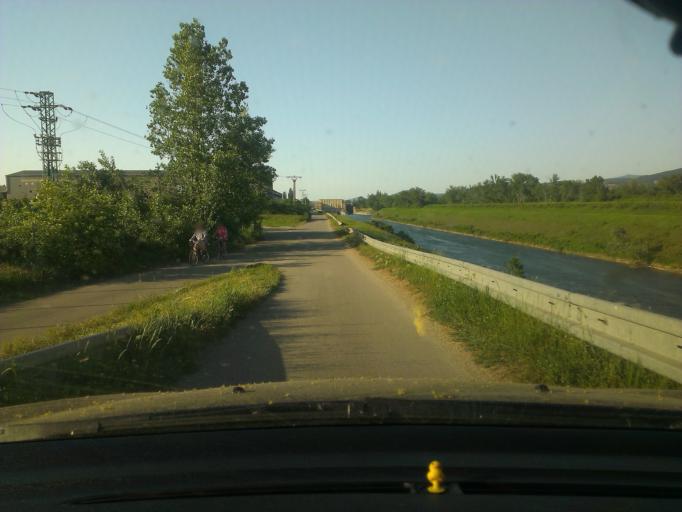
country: SK
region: Trnavsky
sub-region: Okres Trnava
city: Piestany
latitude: 48.6523
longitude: 17.8510
